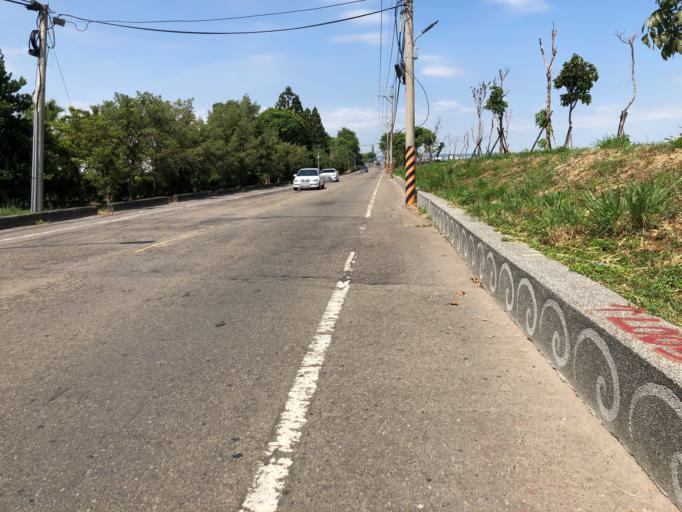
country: TW
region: Taiwan
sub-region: Taichung City
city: Taichung
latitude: 24.0794
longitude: 120.7020
